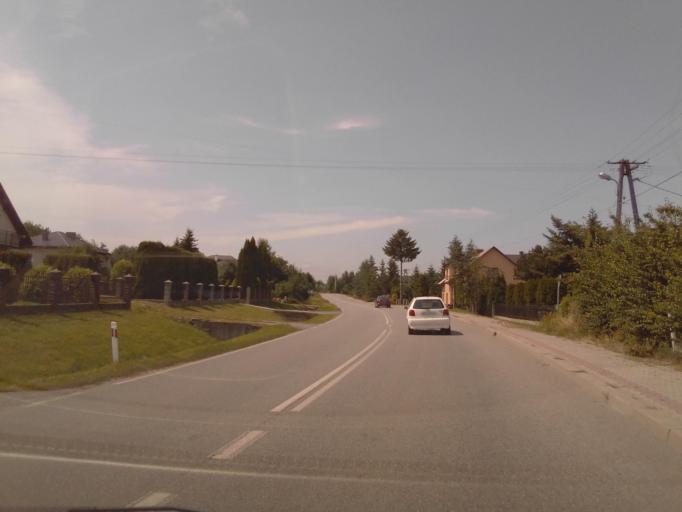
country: PL
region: Subcarpathian Voivodeship
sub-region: Powiat ropczycko-sedziszowski
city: Ropczyce
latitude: 50.0485
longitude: 21.5999
